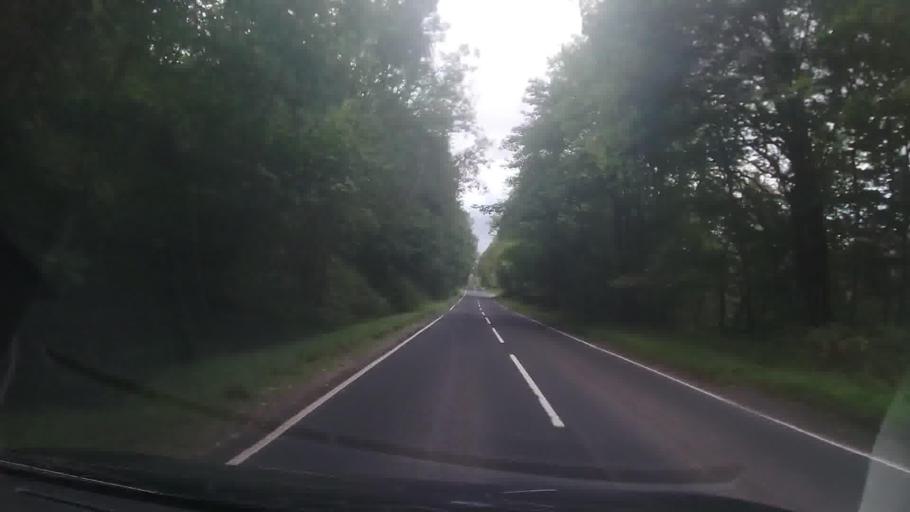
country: GB
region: Scotland
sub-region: Argyll and Bute
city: Garelochhead
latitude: 56.2463
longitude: -4.9315
